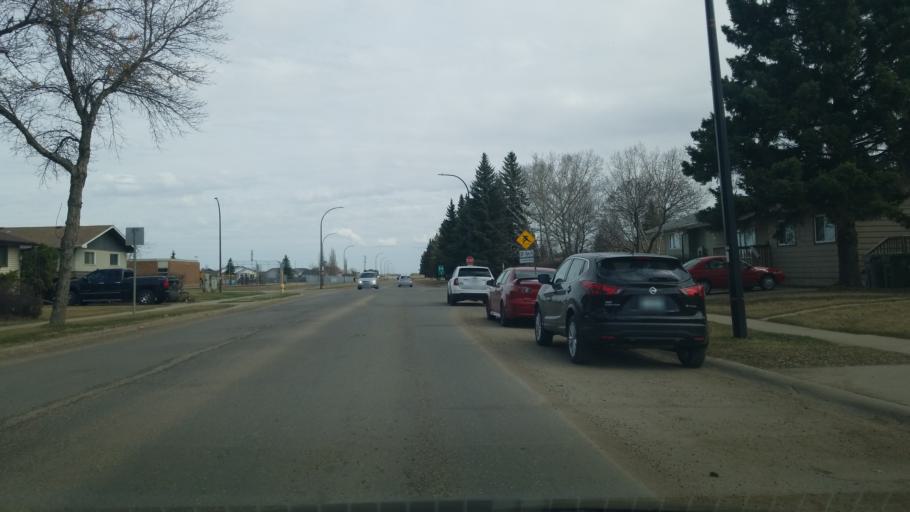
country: CA
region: Saskatchewan
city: Lloydminster
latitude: 53.2707
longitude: -109.9985
